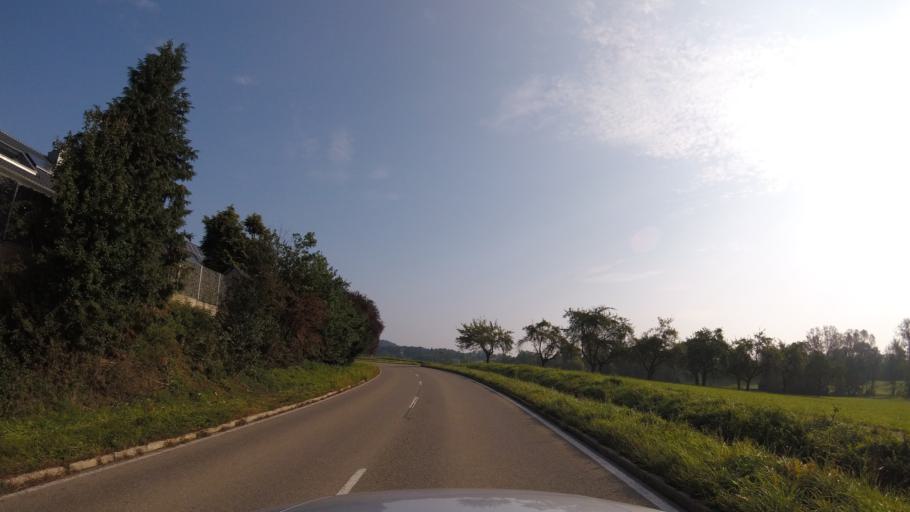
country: DE
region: Baden-Wuerttemberg
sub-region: Regierungsbezirk Stuttgart
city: Aspach
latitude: 48.9744
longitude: 9.4012
